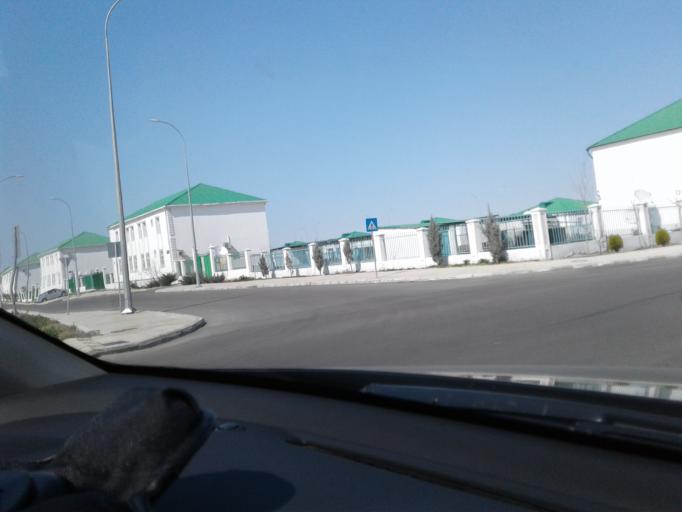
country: TM
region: Ahal
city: Abadan
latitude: 38.0774
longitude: 58.2844
